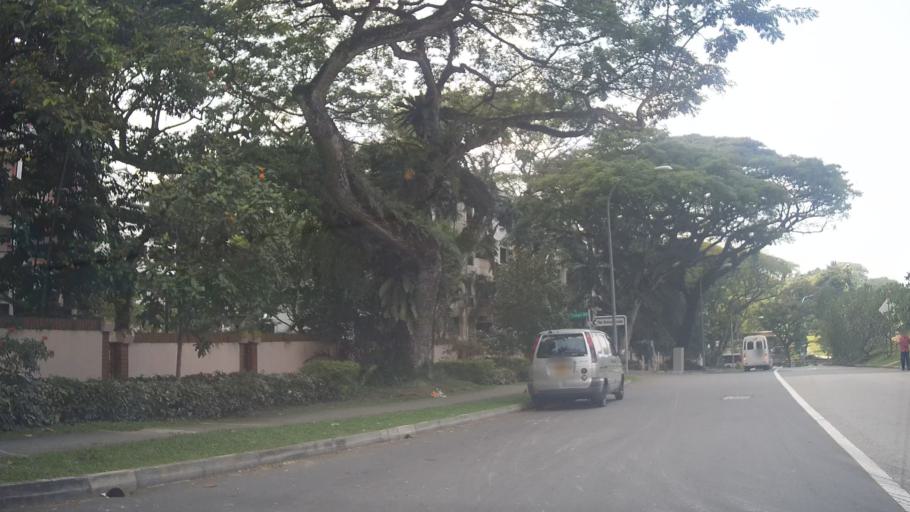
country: SG
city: Singapore
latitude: 1.3383
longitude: 103.7810
